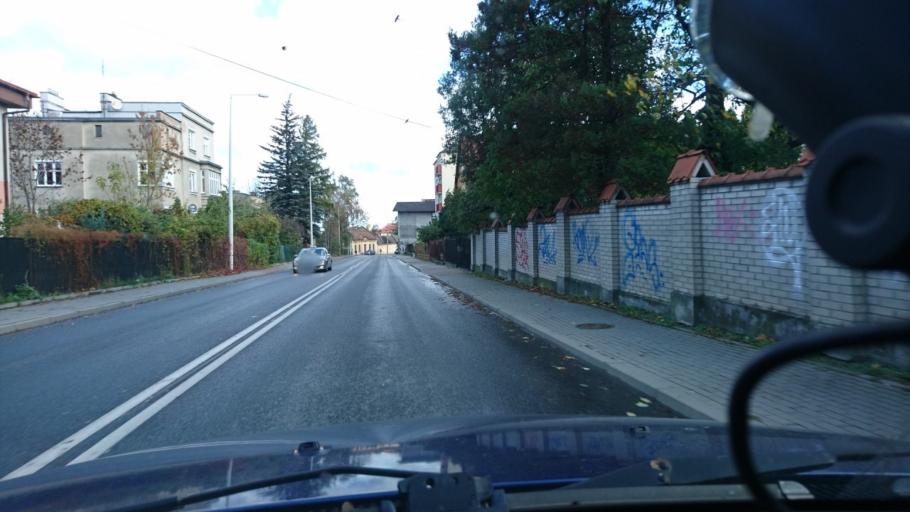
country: PL
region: Silesian Voivodeship
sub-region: Bielsko-Biala
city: Bielsko-Biala
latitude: 49.8213
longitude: 19.0310
